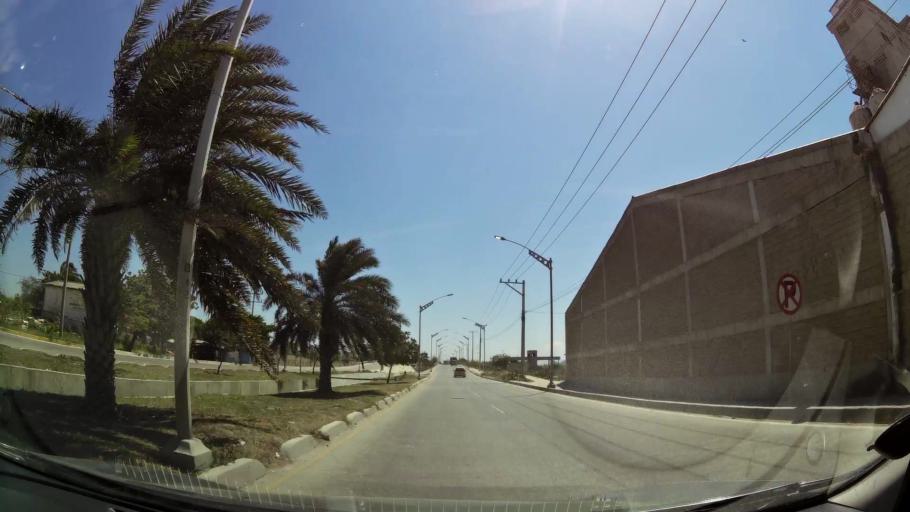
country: CO
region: Atlantico
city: Barranquilla
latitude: 10.9794
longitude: -74.7697
